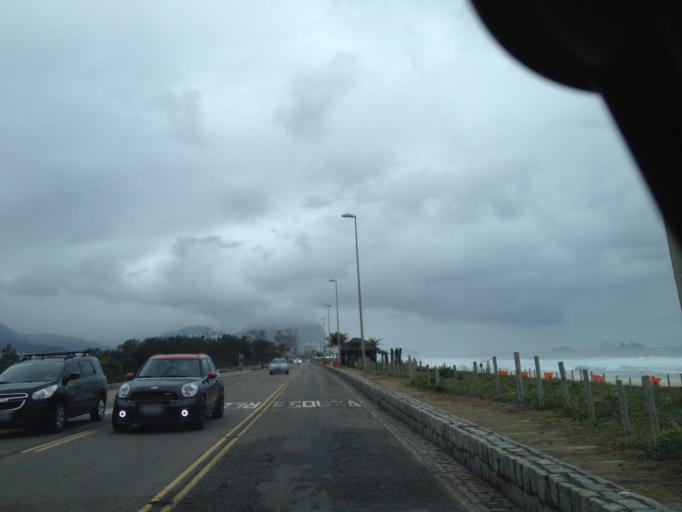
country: BR
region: Rio de Janeiro
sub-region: Rio De Janeiro
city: Rio de Janeiro
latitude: -23.0119
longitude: -43.3809
